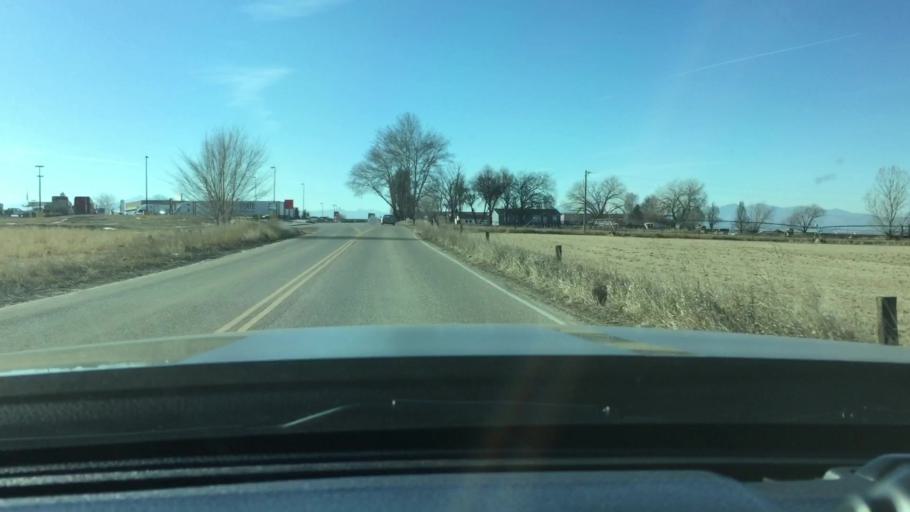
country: US
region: Colorado
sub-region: Weld County
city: Johnstown
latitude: 40.3637
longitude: -104.9797
